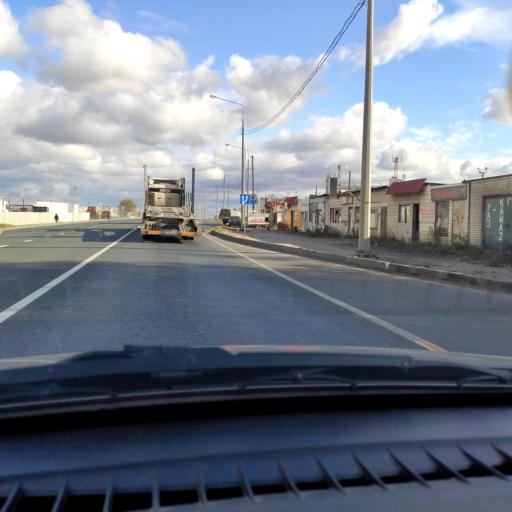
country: RU
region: Samara
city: Varlamovo
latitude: 53.1928
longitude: 48.3605
